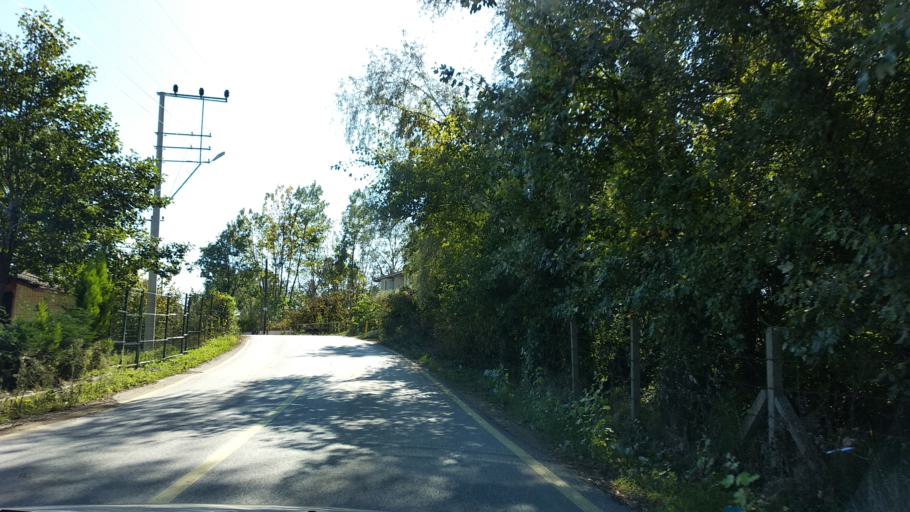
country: TR
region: Sakarya
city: Karasu
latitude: 41.1170
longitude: 30.6445
